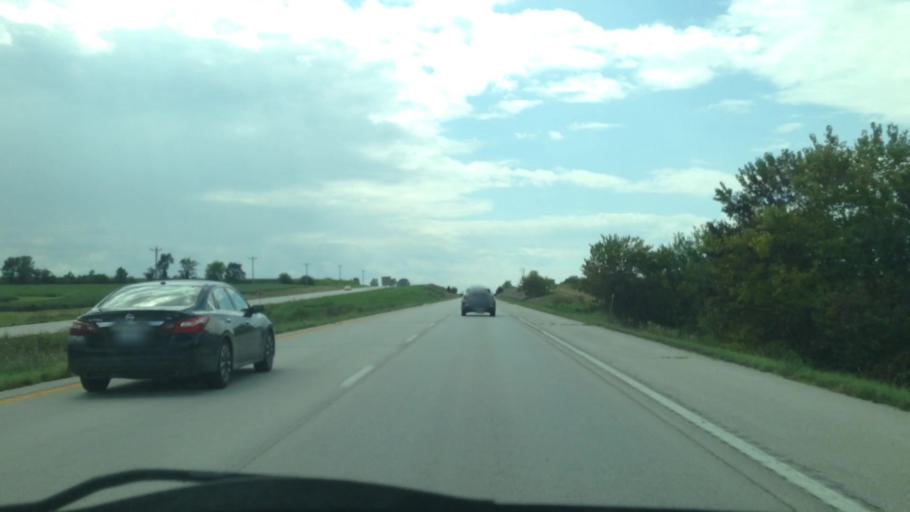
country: US
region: Missouri
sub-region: Marion County
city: Palmyra
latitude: 39.7441
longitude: -91.4570
